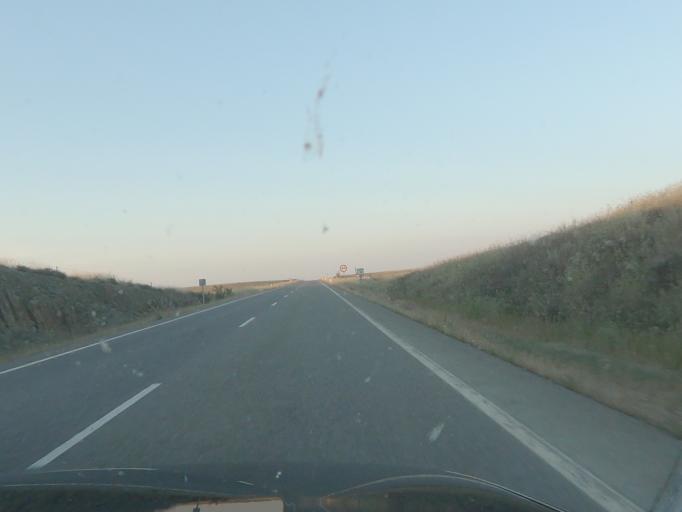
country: ES
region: Extremadura
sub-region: Provincia de Caceres
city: Alcantara
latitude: 39.6197
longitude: -6.9392
